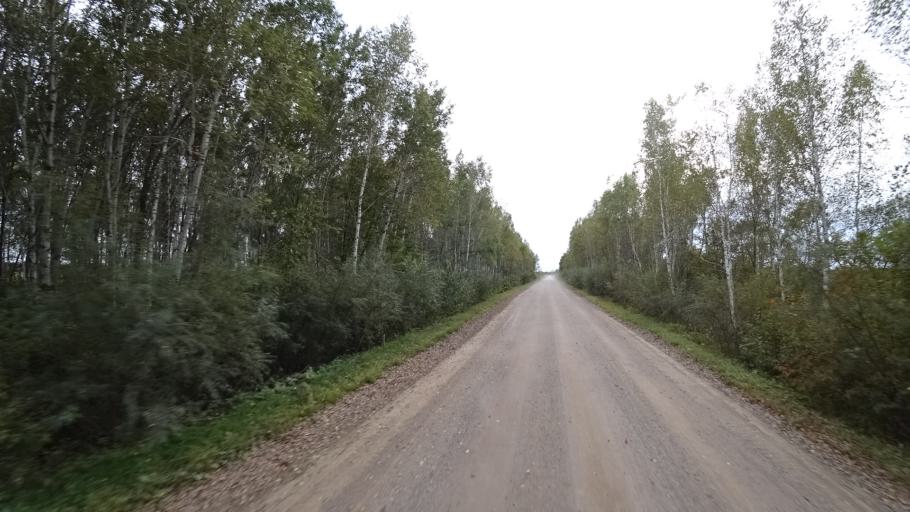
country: RU
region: Amur
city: Arkhara
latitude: 49.3804
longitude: 130.2158
